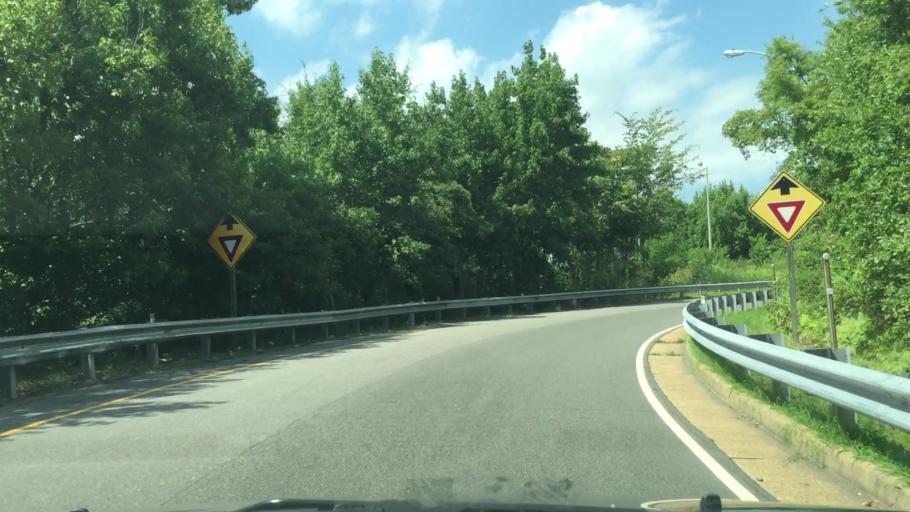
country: US
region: Virginia
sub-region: City of Portsmouth
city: Portsmouth
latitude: 36.8370
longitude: -76.3298
